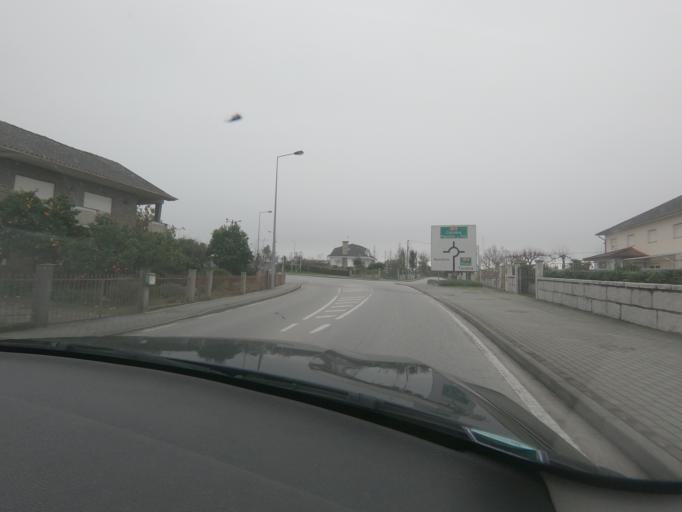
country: PT
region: Viseu
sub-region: Concelho de Tondela
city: Tondela
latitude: 40.5279
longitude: -8.0900
